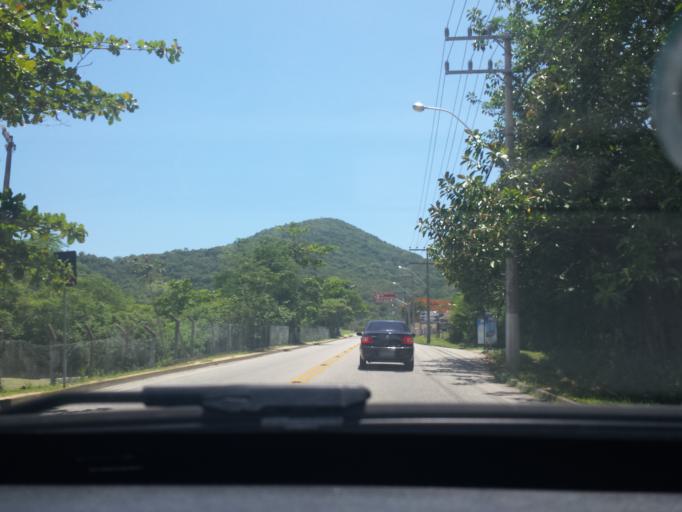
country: BR
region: Santa Catarina
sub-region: Porto Belo
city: Porto Belo
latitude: -27.1453
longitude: -48.5314
